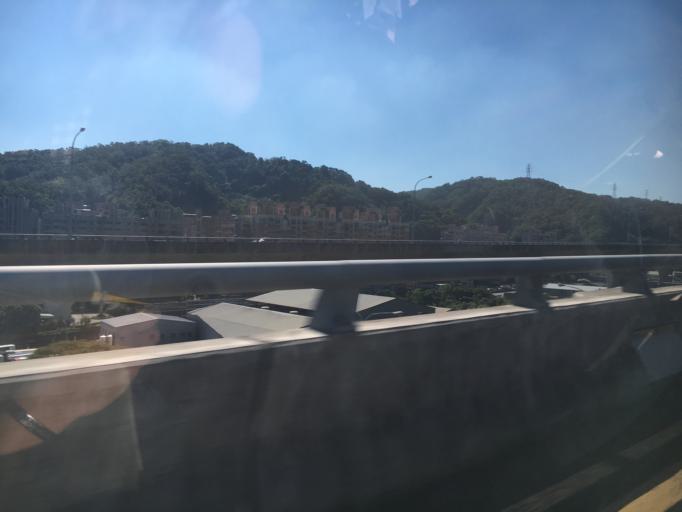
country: TW
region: Taipei
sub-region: Taipei
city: Banqiao
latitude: 25.0675
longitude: 121.4246
